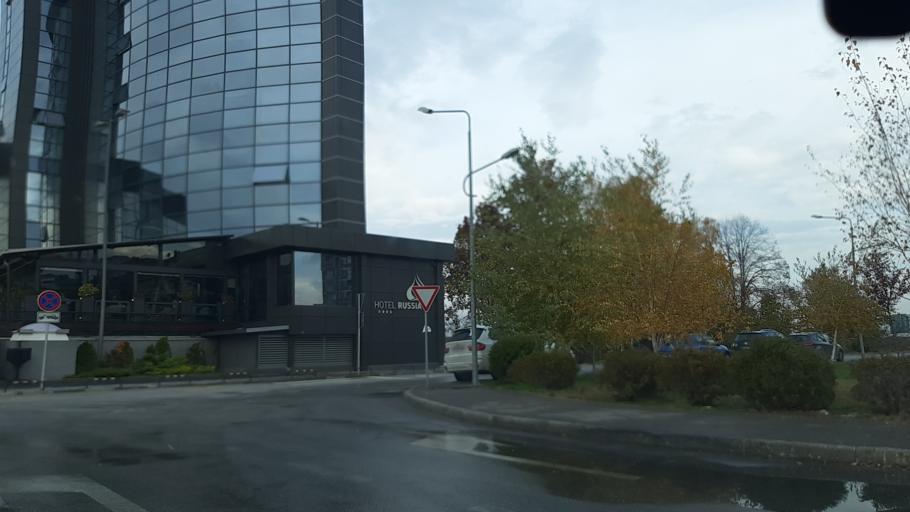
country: MK
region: Cair
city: Cair
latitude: 41.9924
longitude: 21.4650
